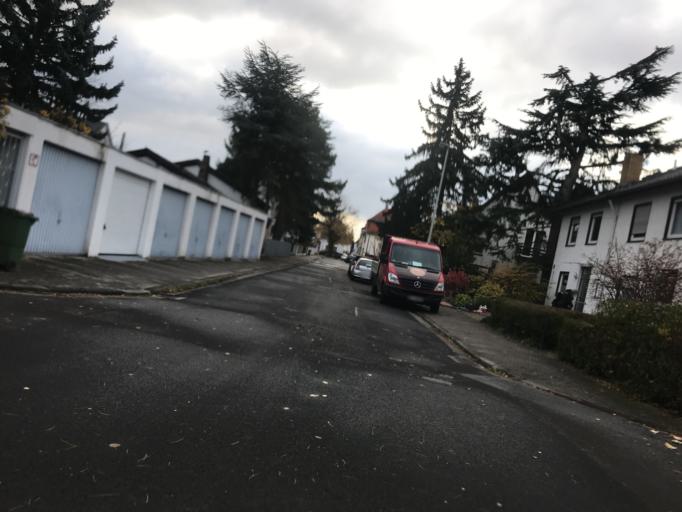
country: DE
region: Rheinland-Pfalz
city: Budenheim
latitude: 50.0064
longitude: 8.2087
